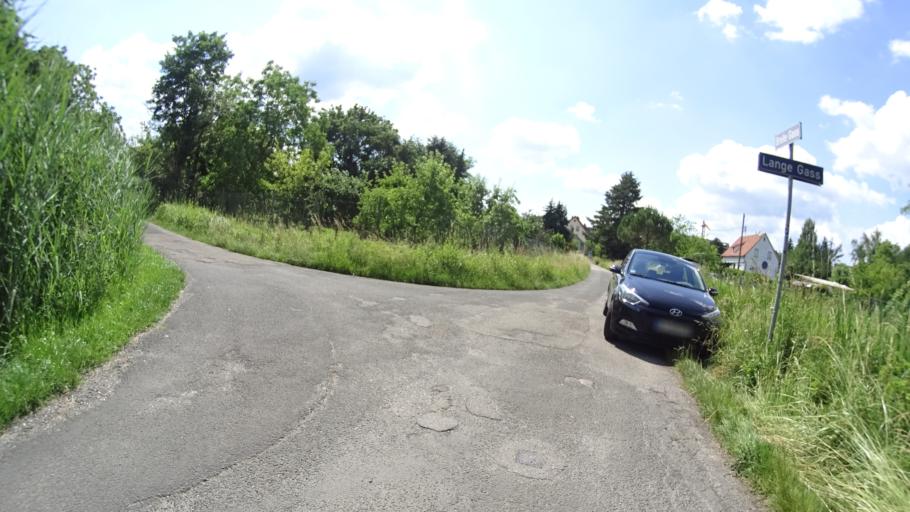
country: DE
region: Baden-Wuerttemberg
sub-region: Karlsruhe Region
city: Karlsruhe
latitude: 48.9945
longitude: 8.4714
